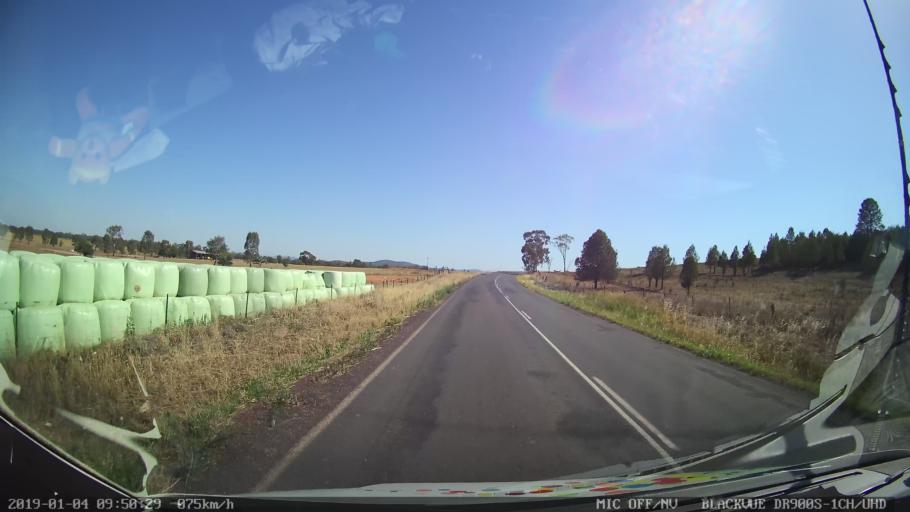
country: AU
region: New South Wales
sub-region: Cabonne
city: Canowindra
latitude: -33.5837
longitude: 148.4155
